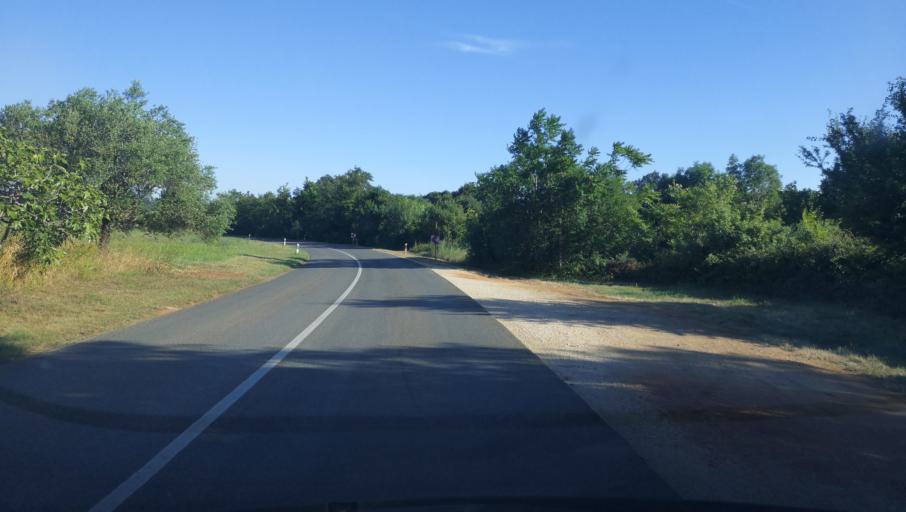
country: HR
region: Istarska
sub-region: Grad Rovinj
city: Rovinj
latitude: 45.0724
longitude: 13.6796
